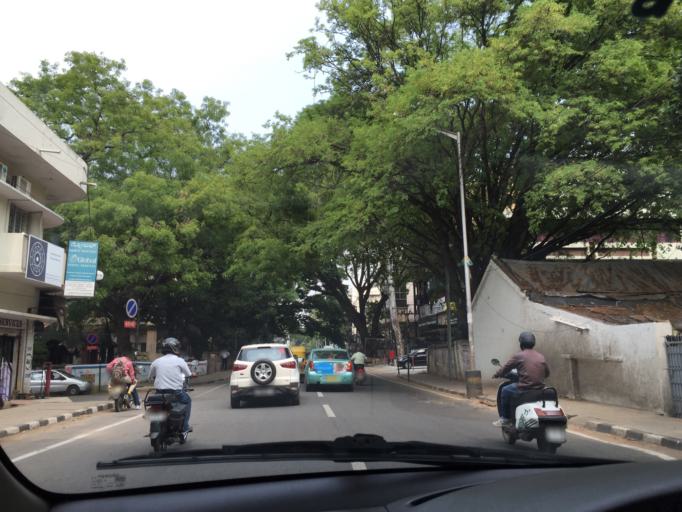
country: IN
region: Karnataka
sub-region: Bangalore Urban
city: Bangalore
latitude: 12.9819
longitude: 77.5995
